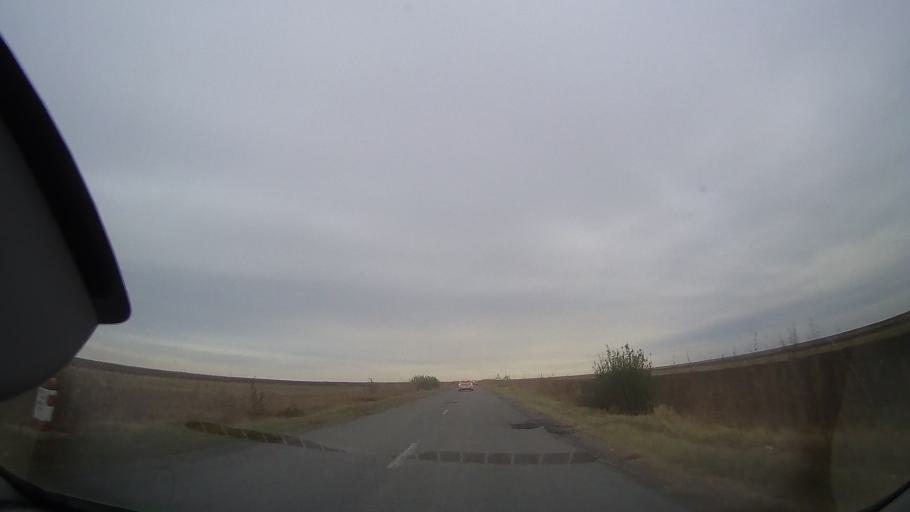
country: RO
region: Ialomita
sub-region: Oras Amara
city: Amara
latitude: 44.6617
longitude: 27.3007
